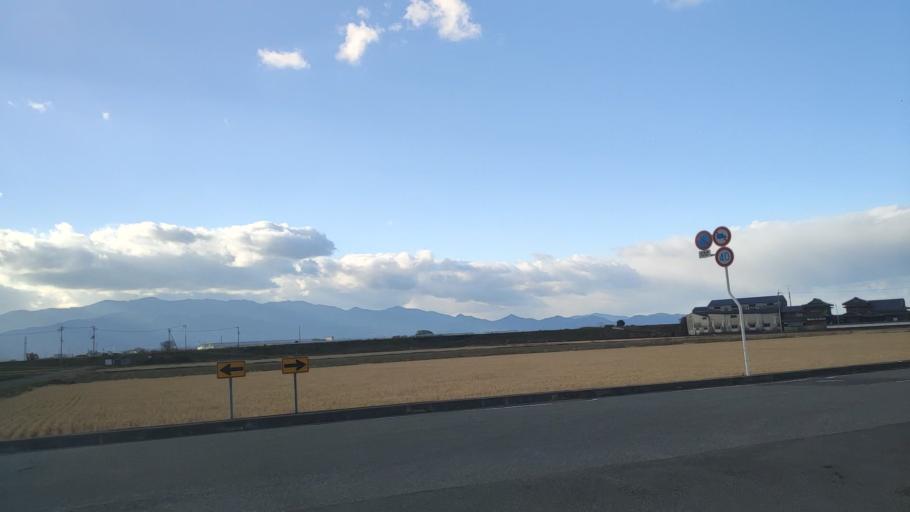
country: JP
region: Ehime
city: Saijo
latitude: 33.9044
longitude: 133.1293
